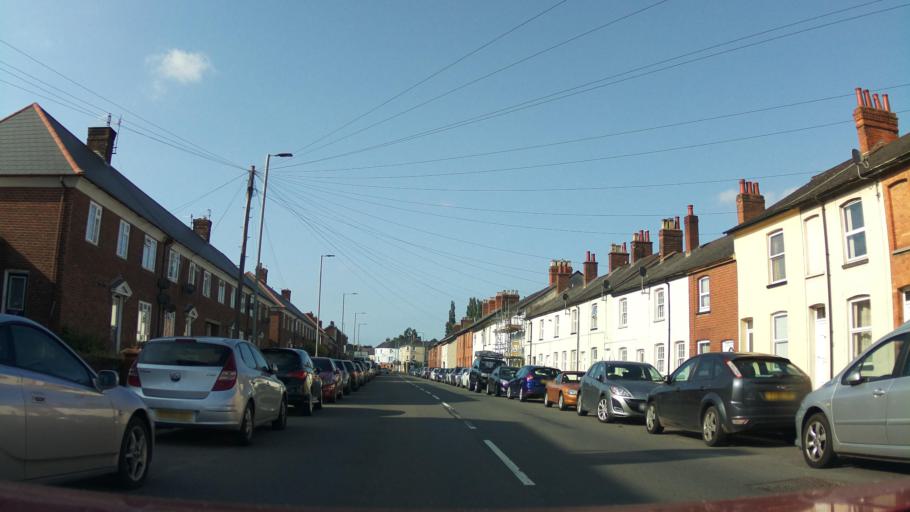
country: GB
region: England
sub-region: Devon
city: Tiverton
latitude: 50.9007
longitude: -3.4911
